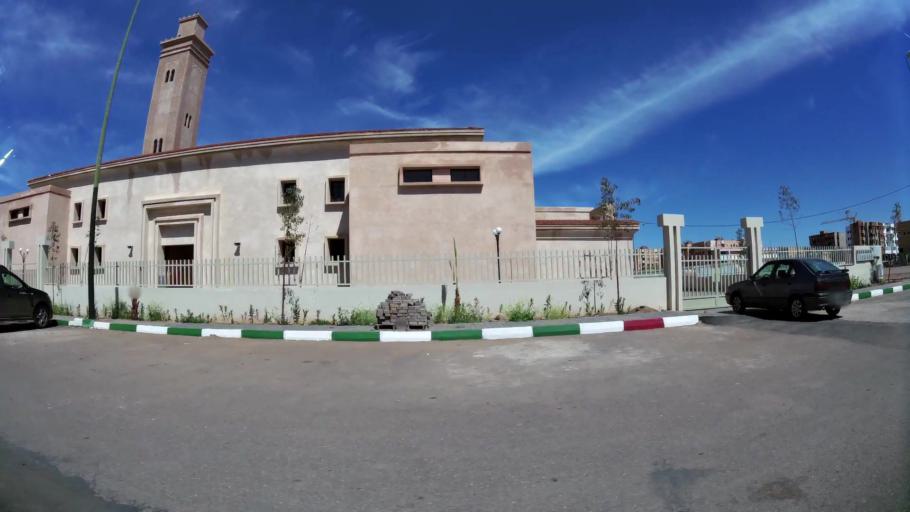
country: MA
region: Marrakech-Tensift-Al Haouz
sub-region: Marrakech
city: Marrakesh
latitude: 31.6369
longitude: -8.0758
